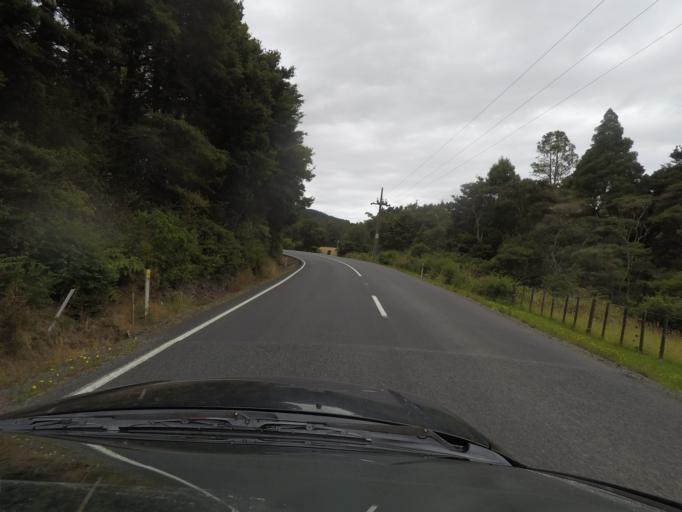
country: NZ
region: Auckland
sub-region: Auckland
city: Wellsford
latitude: -36.2866
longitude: 174.6129
